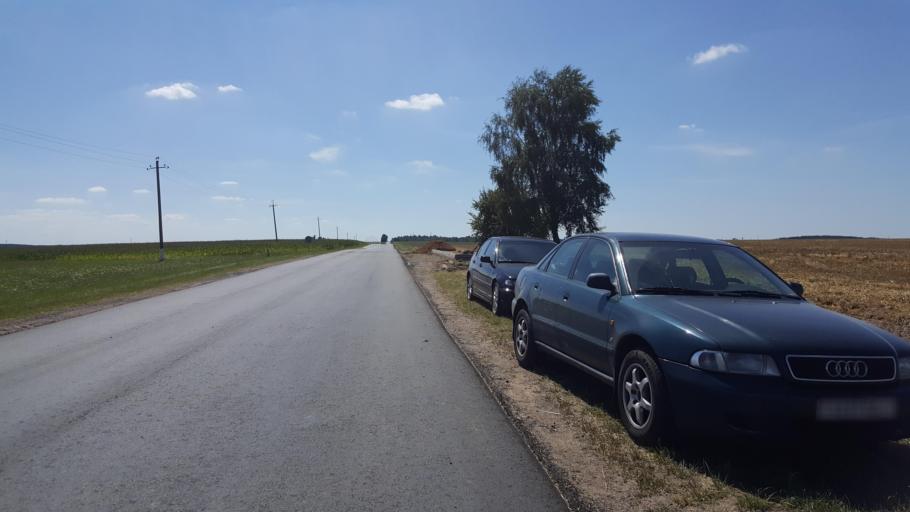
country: BY
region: Brest
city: Charnawchytsy
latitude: 52.2968
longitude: 23.6068
